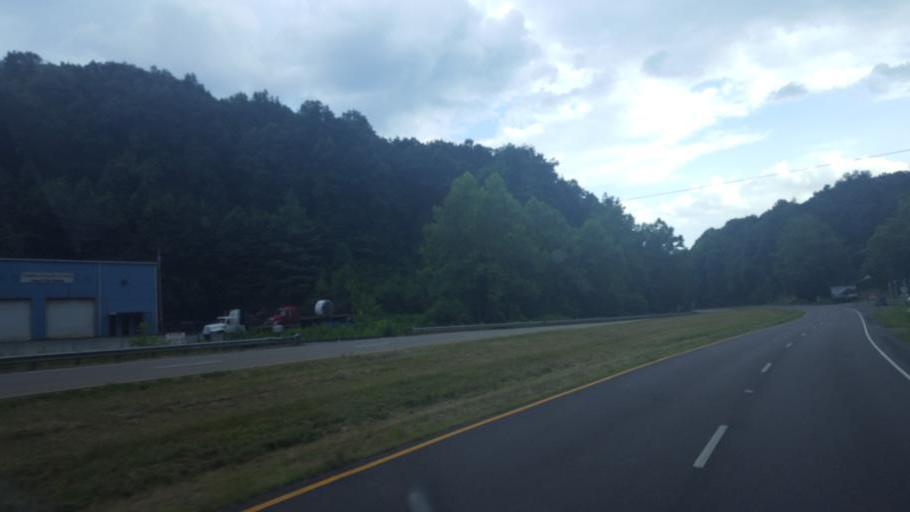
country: US
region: Virginia
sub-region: Wise County
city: Pound
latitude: 37.0730
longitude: -82.5995
